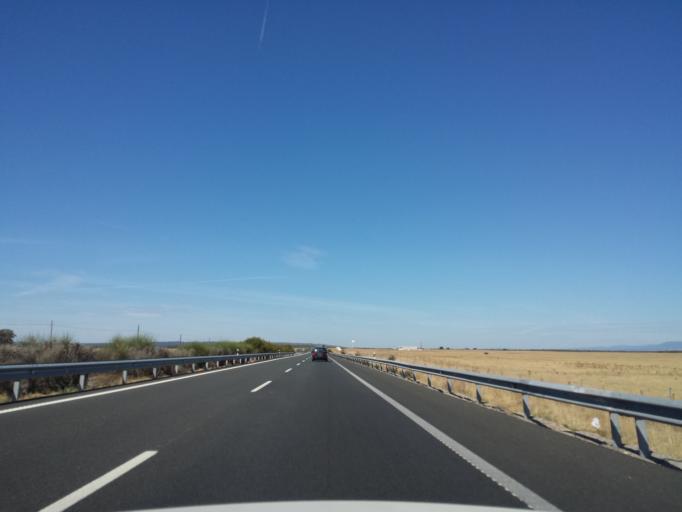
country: ES
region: Extremadura
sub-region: Provincia de Caceres
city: Peraleda de la Mata
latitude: 39.8917
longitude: -5.4035
